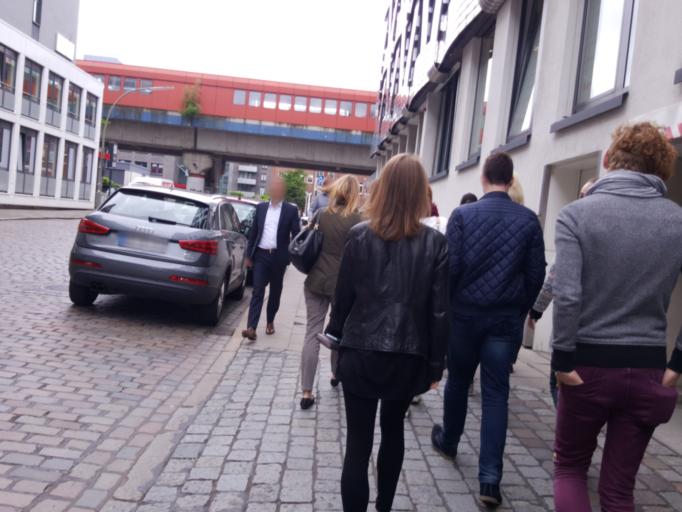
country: DE
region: Hamburg
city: Hammerbrook
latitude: 53.5468
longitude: 10.0248
